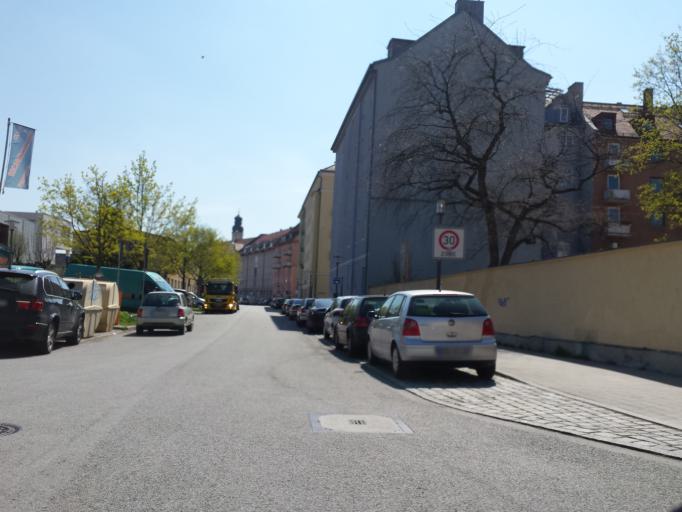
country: DE
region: Bavaria
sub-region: Upper Bavaria
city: Munich
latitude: 48.1208
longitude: 11.5503
